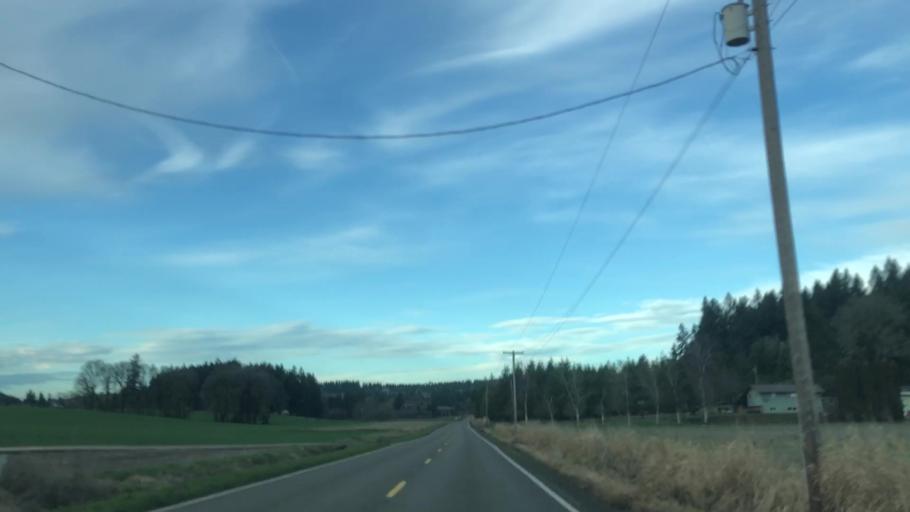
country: US
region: Oregon
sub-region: Washington County
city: Rockcreek
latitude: 45.5868
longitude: -122.9192
